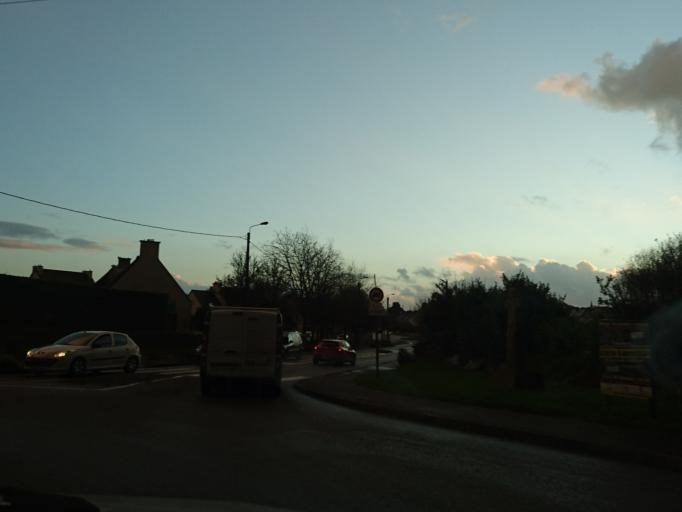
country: FR
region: Brittany
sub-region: Departement du Finistere
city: Guipavas
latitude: 48.4409
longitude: -4.3945
